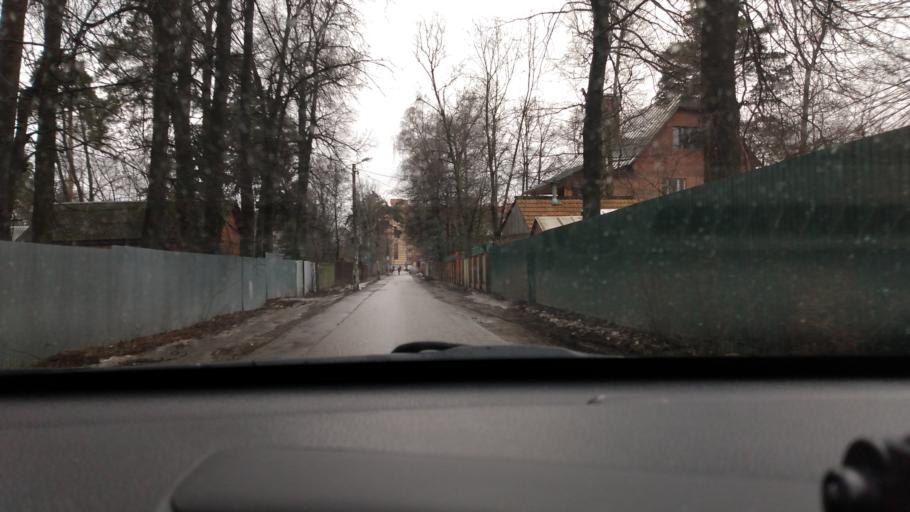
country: RU
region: Moskovskaya
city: Druzhba
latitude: 55.8984
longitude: 37.7425
